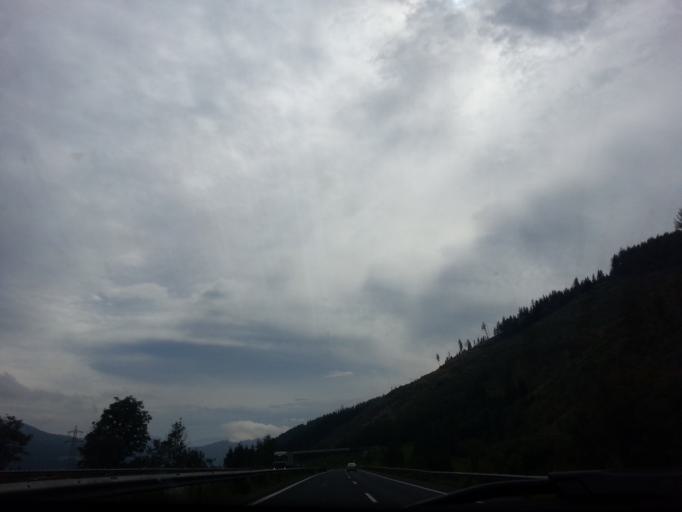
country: AT
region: Styria
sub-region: Politischer Bezirk Leoben
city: Kammern im Liesingtal
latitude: 47.3861
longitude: 14.9181
